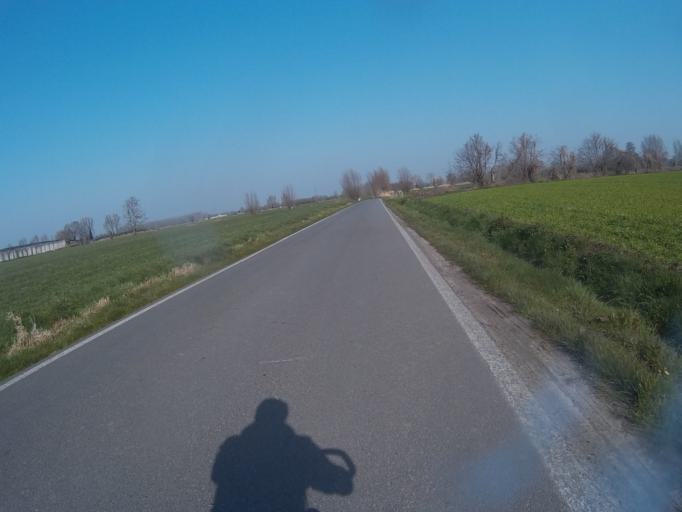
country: BE
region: Flanders
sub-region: Provincie Oost-Vlaanderen
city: Zomergem
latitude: 51.1064
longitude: 3.5115
